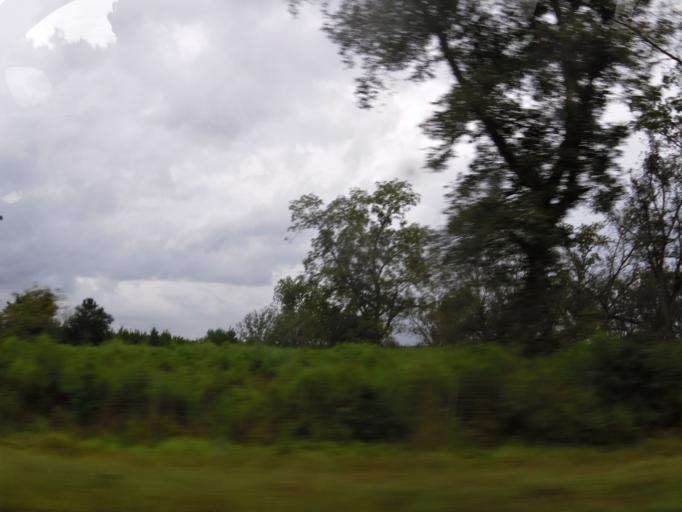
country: US
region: Georgia
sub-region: Wayne County
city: Jesup
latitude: 31.5605
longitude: -81.8323
